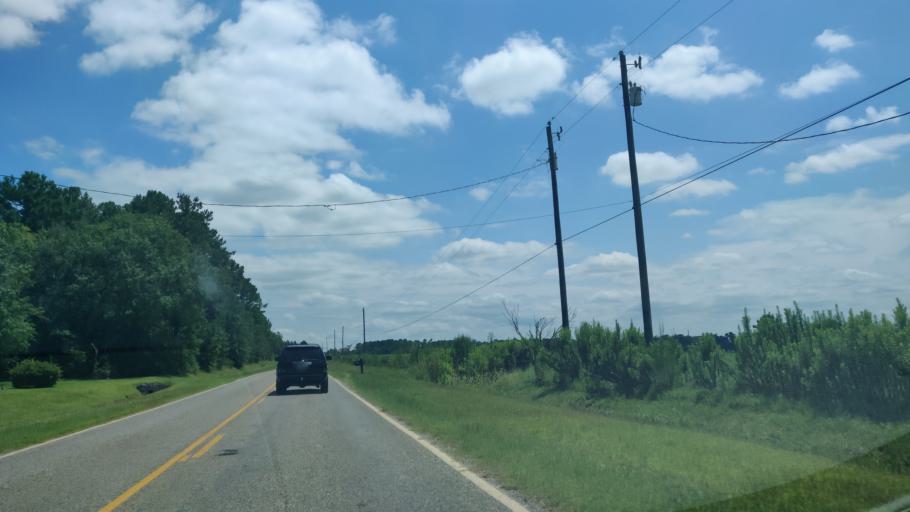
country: US
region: Georgia
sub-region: Tift County
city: Omega
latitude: 31.4348
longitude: -83.6381
